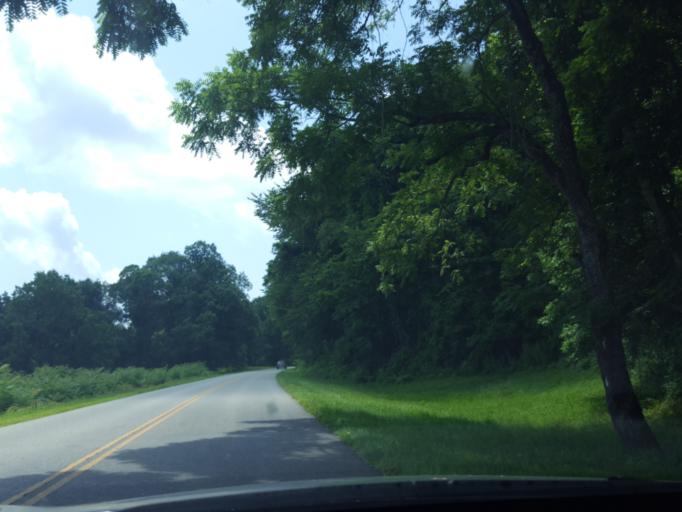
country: US
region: Virginia
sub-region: City of Waynesboro
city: Waynesboro
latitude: 38.0277
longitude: -78.8583
